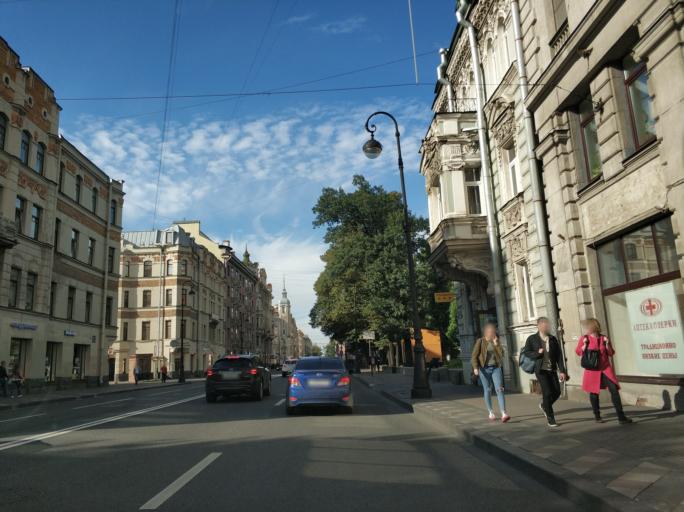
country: RU
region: St.-Petersburg
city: Petrogradka
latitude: 59.9584
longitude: 30.3188
